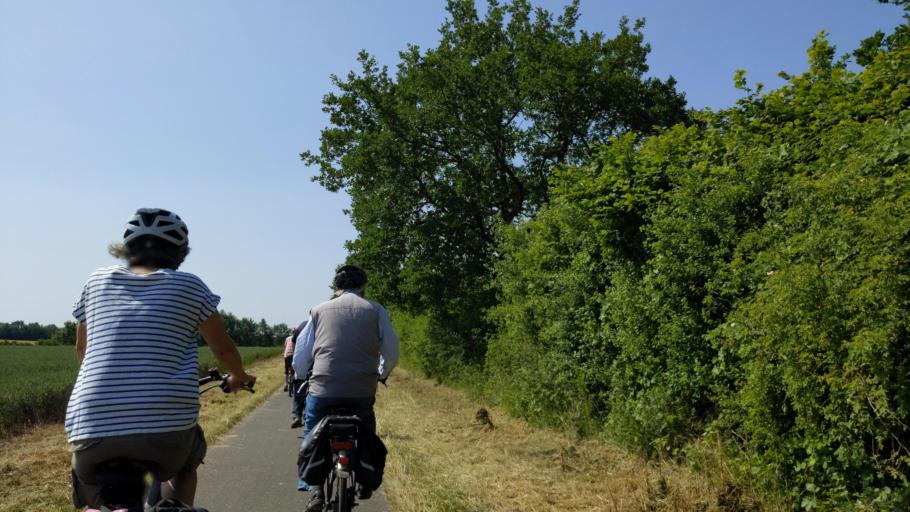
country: DE
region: Schleswig-Holstein
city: Klempau
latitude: 53.7556
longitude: 10.6578
